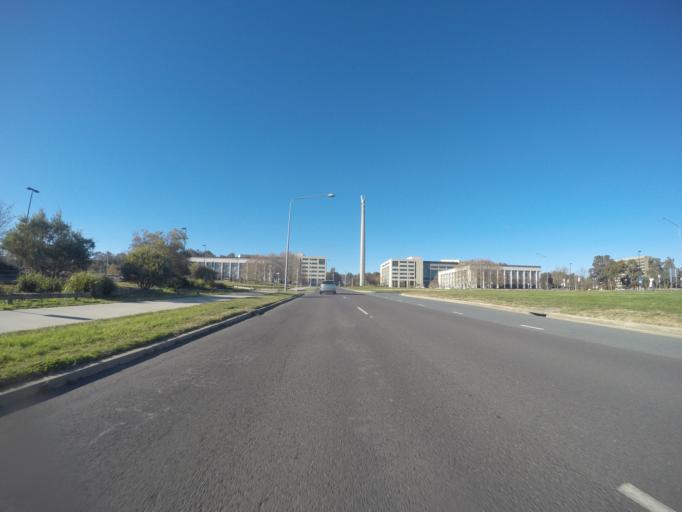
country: AU
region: Australian Capital Territory
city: Canberra
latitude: -35.2983
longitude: 149.1490
